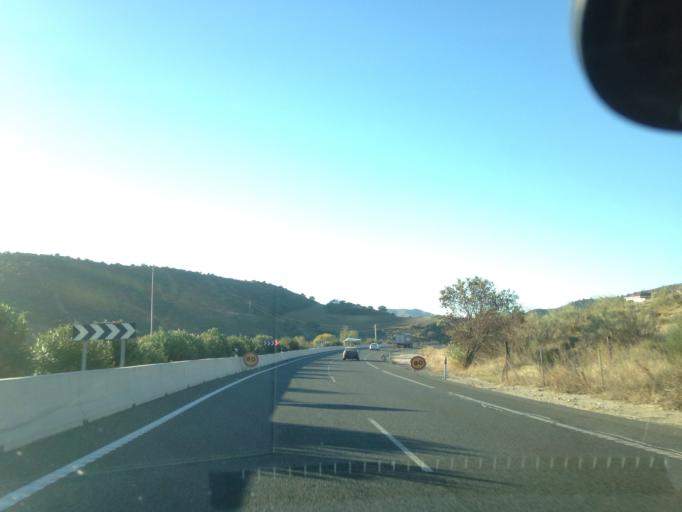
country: ES
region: Andalusia
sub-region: Provincia de Malaga
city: Casabermeja
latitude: 36.9390
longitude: -4.4392
